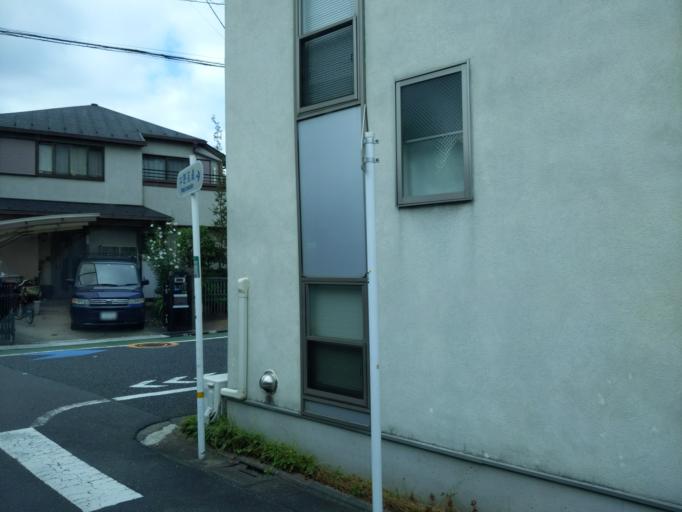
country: JP
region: Kanagawa
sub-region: Kawasaki-shi
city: Kawasaki
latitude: 35.5849
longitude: 139.6938
